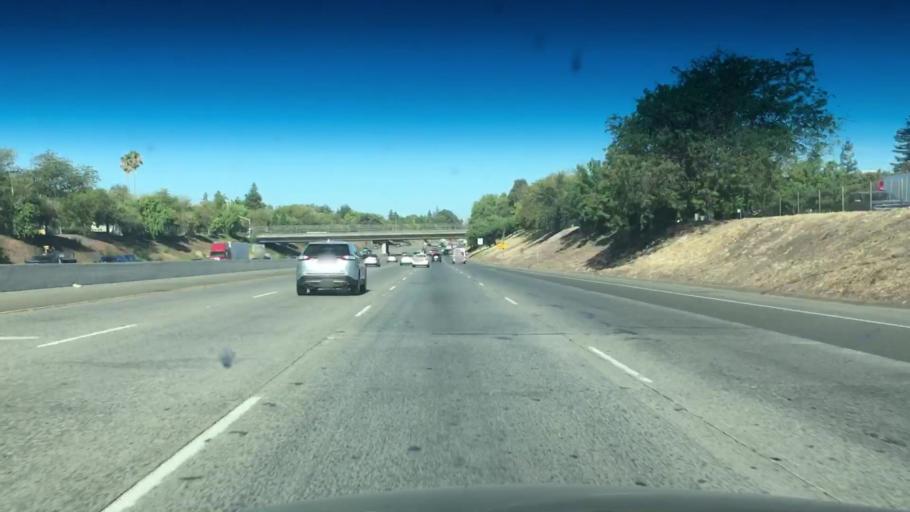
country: US
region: California
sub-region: Sacramento County
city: Florin
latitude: 38.5524
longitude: -121.4338
